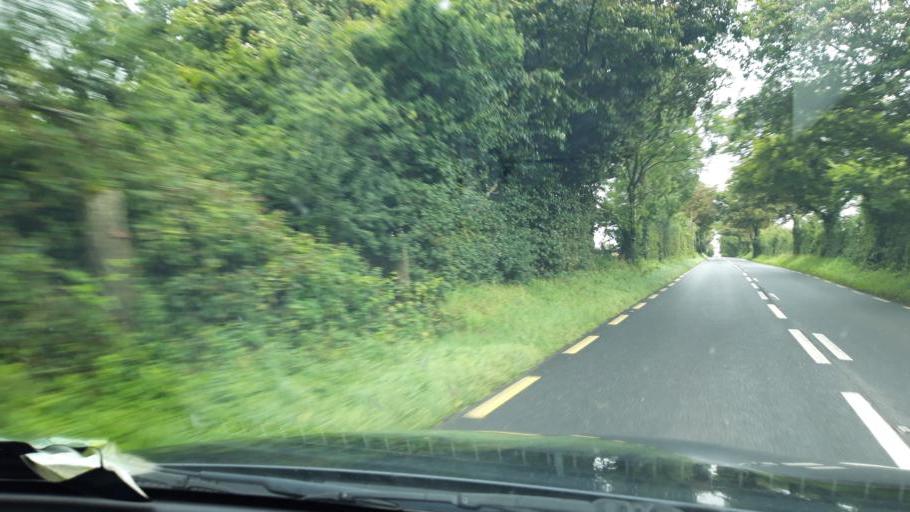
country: IE
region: Leinster
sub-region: Loch Garman
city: New Ross
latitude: 52.4333
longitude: -6.7794
